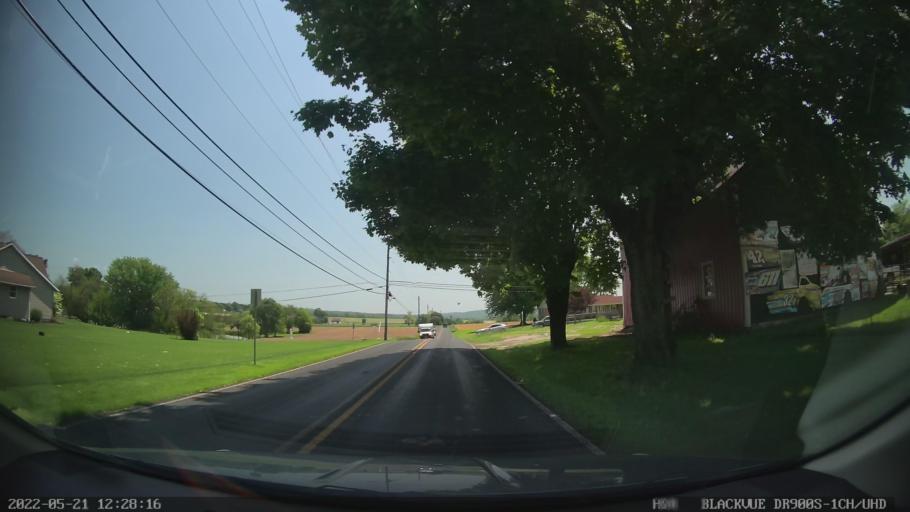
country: US
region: Pennsylvania
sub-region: Berks County
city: Bally
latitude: 40.3700
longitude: -75.5973
